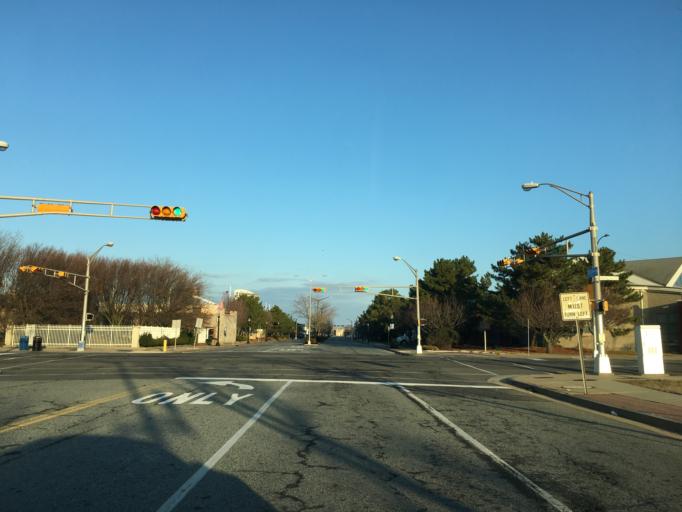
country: US
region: New Jersey
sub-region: Atlantic County
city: Atlantic City
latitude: 39.3649
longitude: -74.4203
